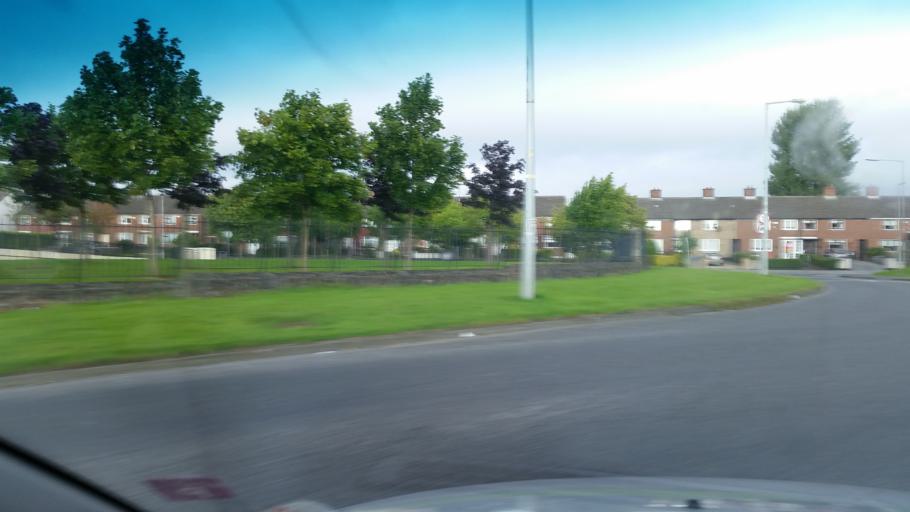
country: IE
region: Leinster
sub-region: Dublin City
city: Finglas
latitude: 53.3962
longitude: -6.3054
